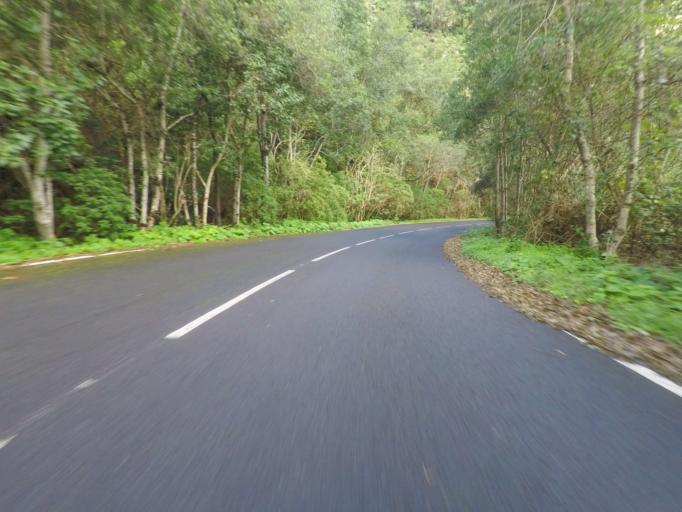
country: ES
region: Canary Islands
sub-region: Provincia de Santa Cruz de Tenerife
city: Hermigua
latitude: 28.1256
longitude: -17.2113
